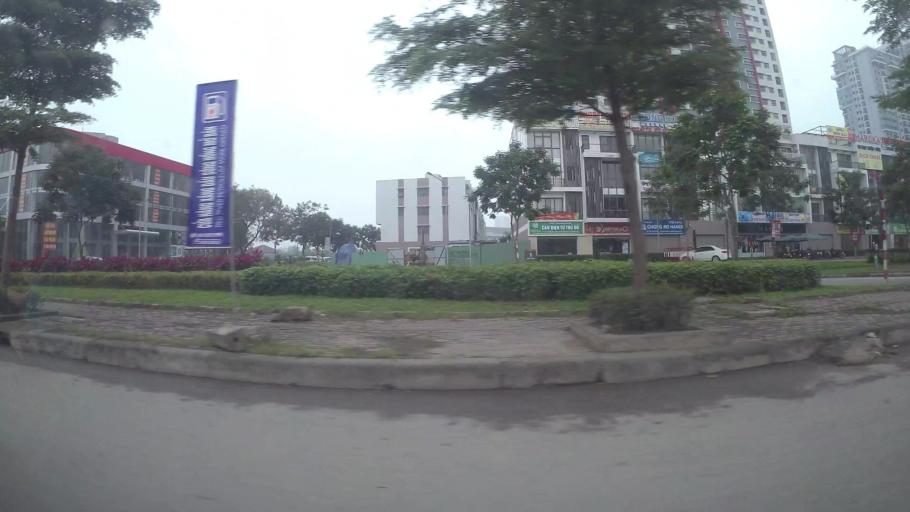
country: VN
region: Ha Noi
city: Van Dien
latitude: 20.9682
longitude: 105.8777
